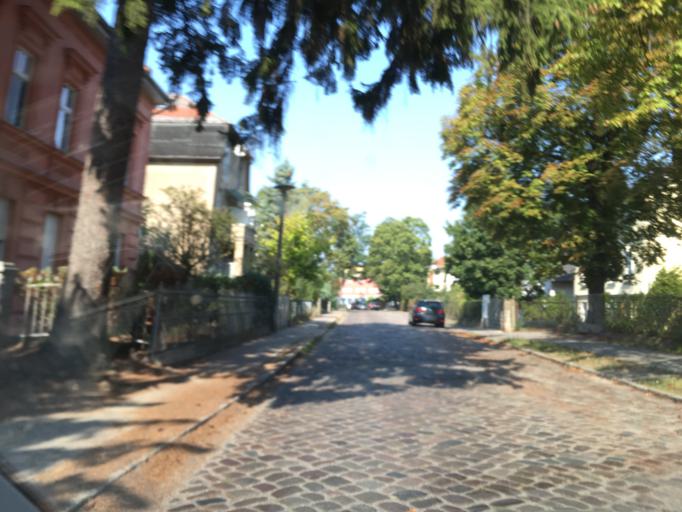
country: DE
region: Berlin
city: Rahnsdorf
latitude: 52.4399
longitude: 13.6881
